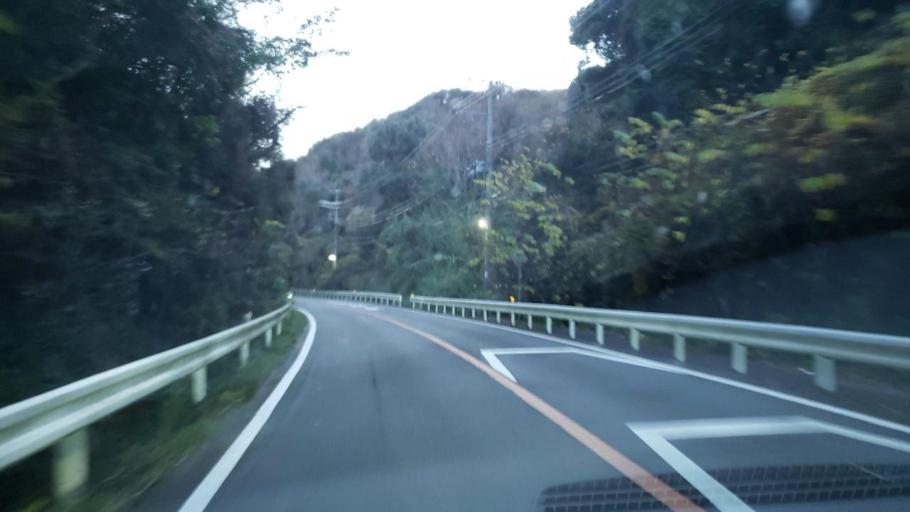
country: JP
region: Hyogo
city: Fukura
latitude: 34.2902
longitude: 134.7124
